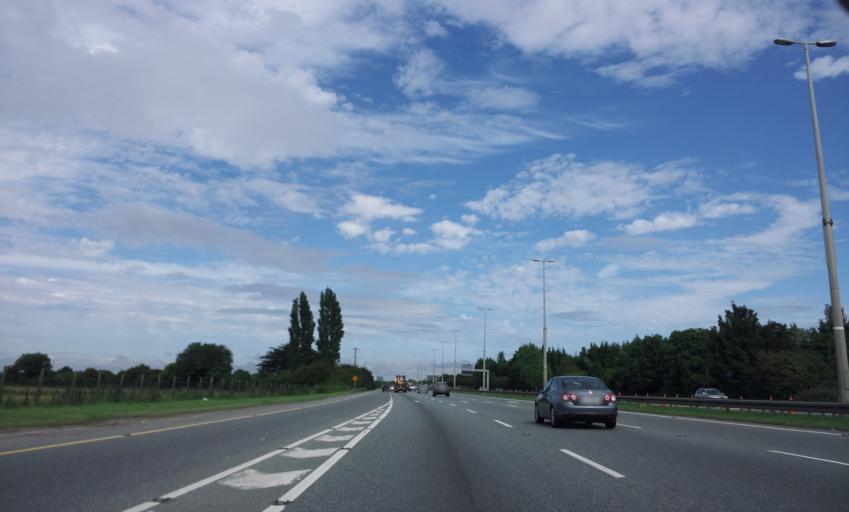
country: IE
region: Leinster
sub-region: South Dublin
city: Saggart
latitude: 53.2854
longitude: -6.4554
